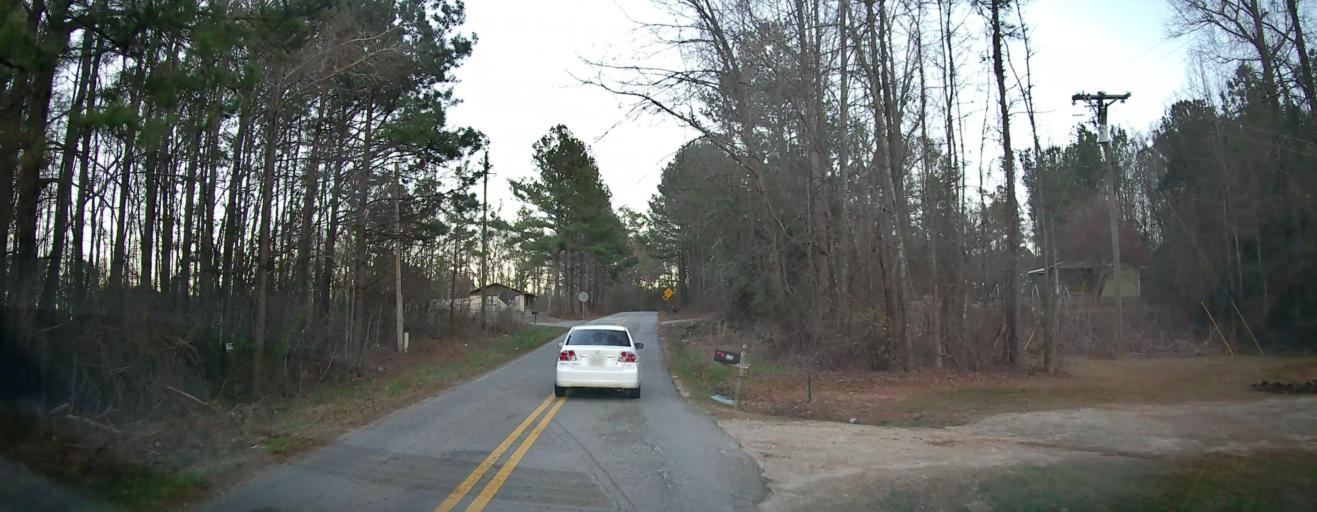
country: US
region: Georgia
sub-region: Troup County
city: La Grange
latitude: 33.0616
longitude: -84.9701
